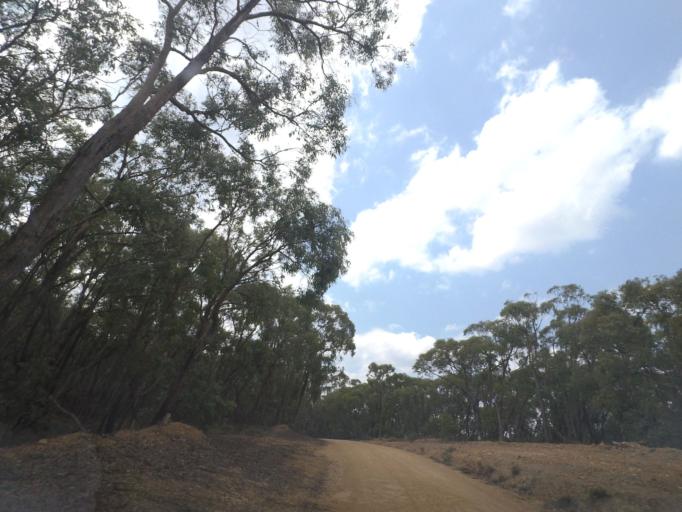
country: AU
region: Victoria
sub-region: Moorabool
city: Bacchus Marsh
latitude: -37.5287
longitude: 144.4348
